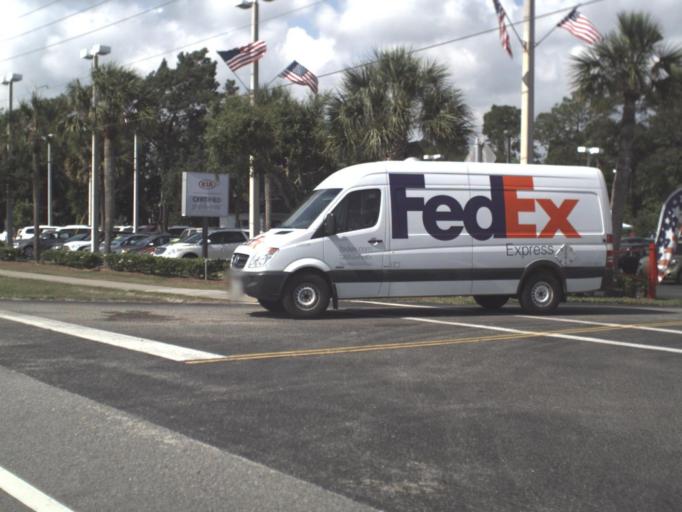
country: US
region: Florida
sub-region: Saint Johns County
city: Saint Augustine South
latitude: 29.8475
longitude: -81.3227
